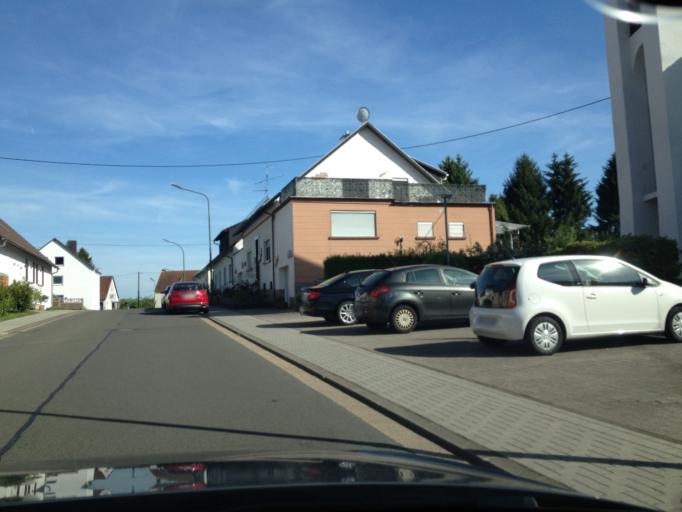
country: DE
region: Saarland
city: Bexbach
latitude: 49.3228
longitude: 7.2395
